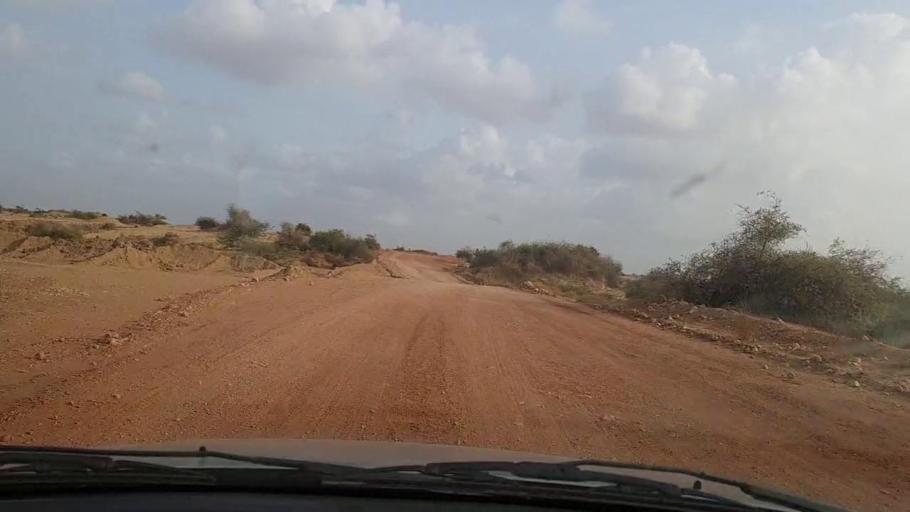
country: PK
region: Sindh
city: Thatta
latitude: 25.0707
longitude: 67.8900
